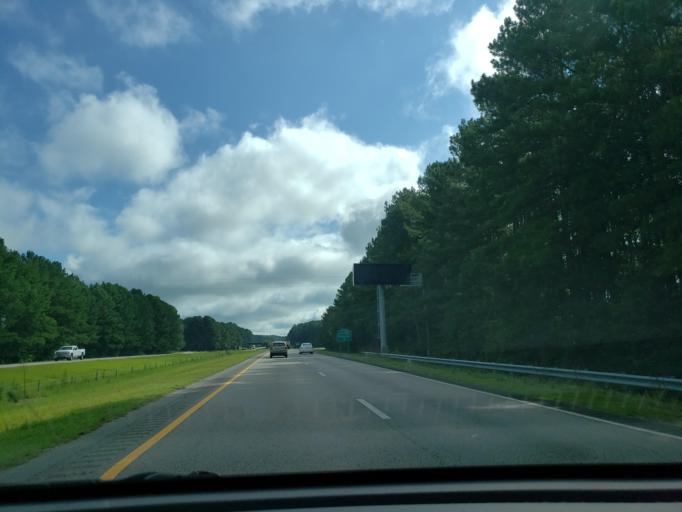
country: US
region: North Carolina
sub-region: Nash County
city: Spring Hope
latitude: 35.9371
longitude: -78.0604
